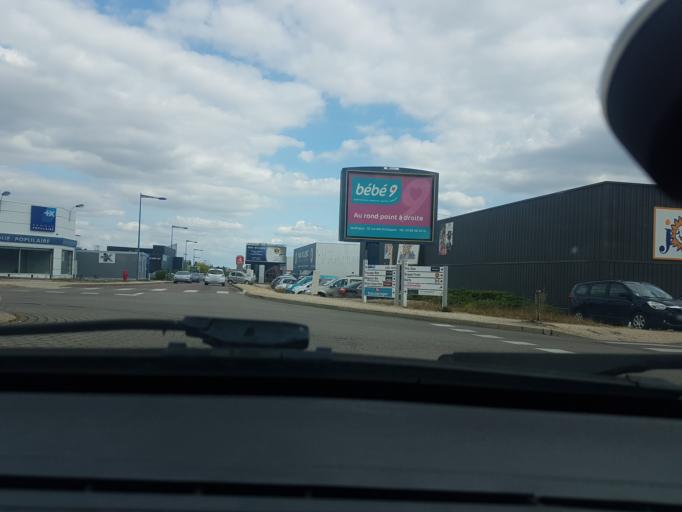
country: FR
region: Bourgogne
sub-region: Departement de la Cote-d'Or
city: Quetigny
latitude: 47.3104
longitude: 5.0953
